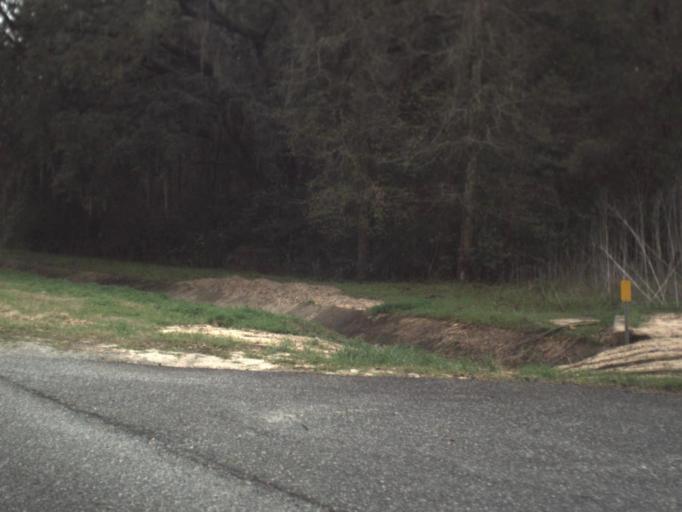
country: US
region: Florida
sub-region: Leon County
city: Tallahassee
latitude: 30.4253
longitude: -84.1803
